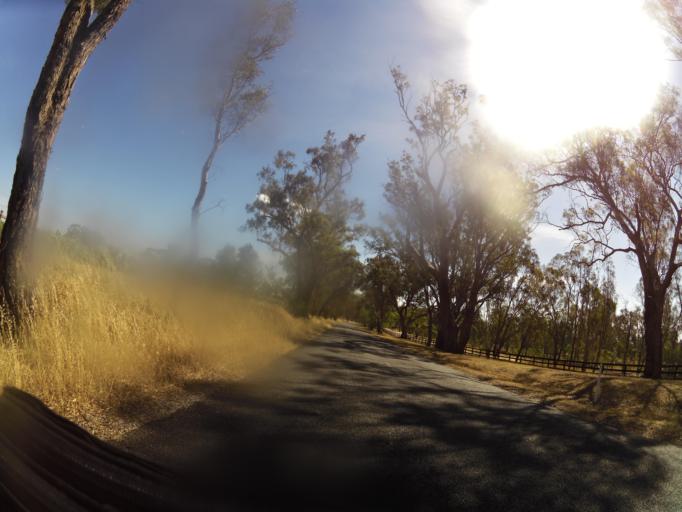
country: AU
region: Victoria
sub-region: Campaspe
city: Kyabram
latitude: -36.8577
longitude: 145.0947
